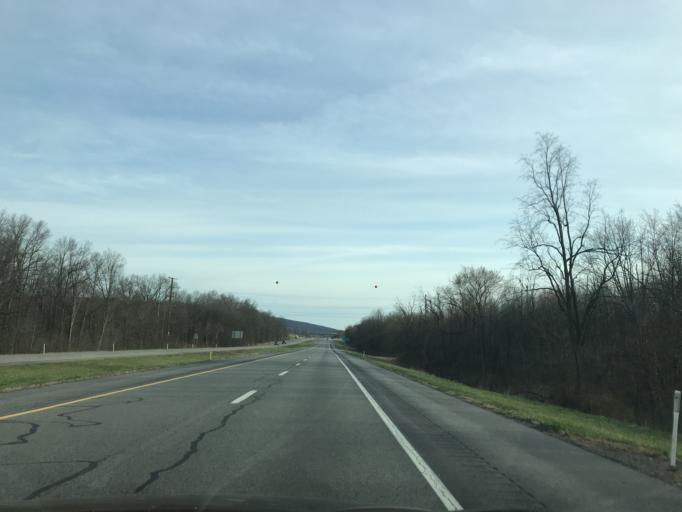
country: US
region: Pennsylvania
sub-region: Northumberland County
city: Milton
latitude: 40.9932
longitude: -76.8372
